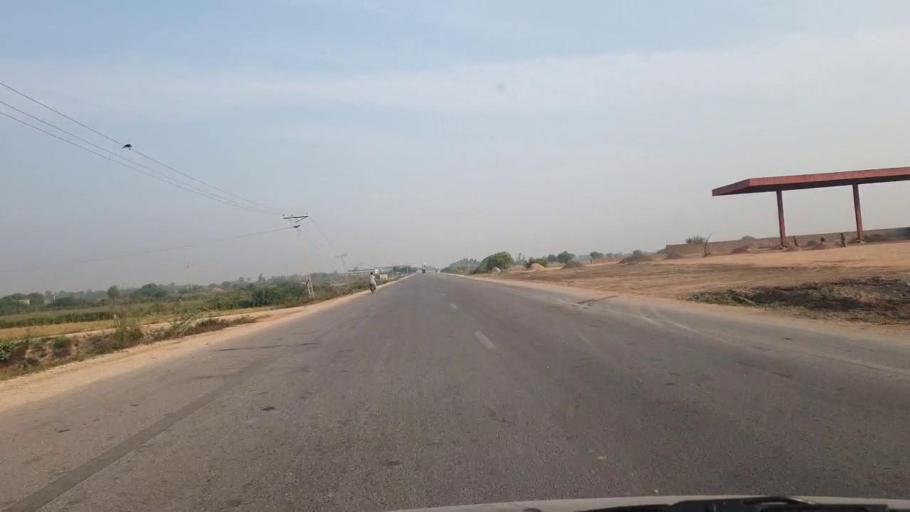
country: PK
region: Sindh
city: Badin
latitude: 24.6889
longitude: 68.8237
